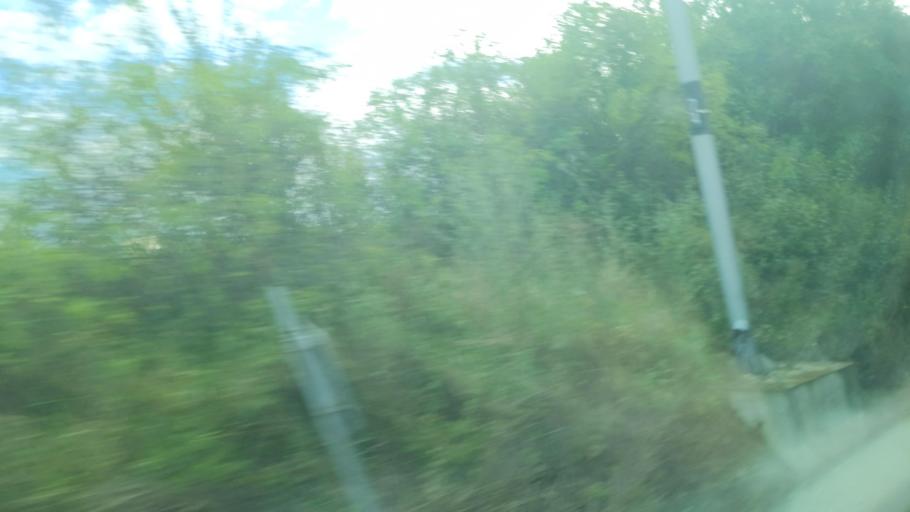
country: CZ
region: Central Bohemia
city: Cesky Brod
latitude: 50.0795
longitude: 14.8217
